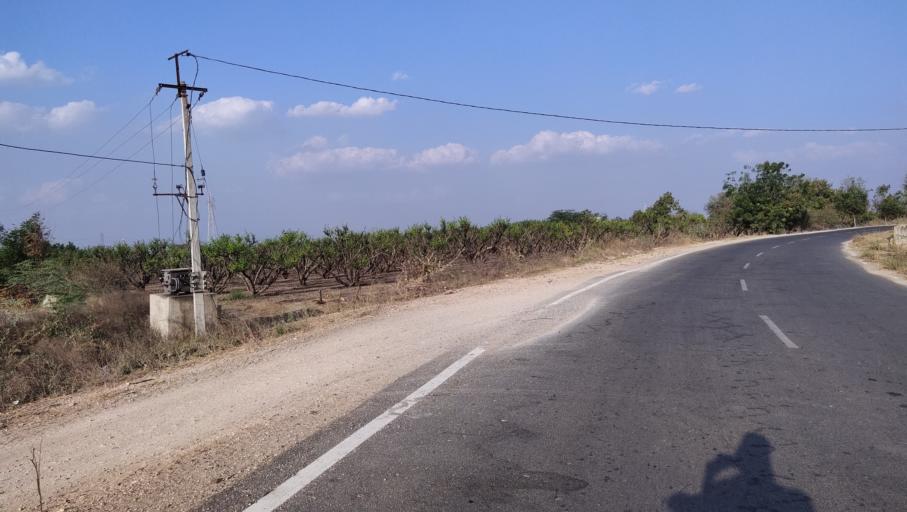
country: IN
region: Andhra Pradesh
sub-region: Anantapur
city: Tadpatri
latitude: 14.9512
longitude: 77.8821
